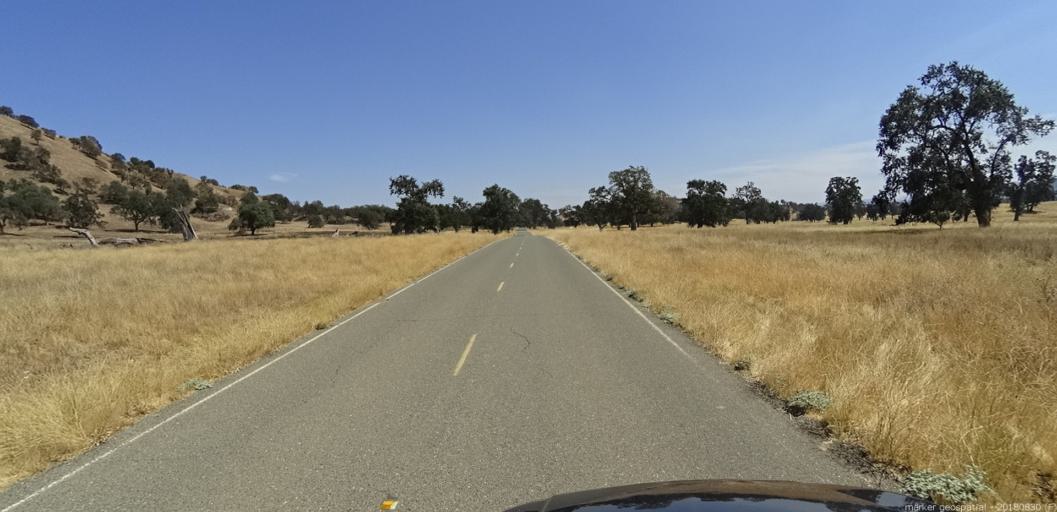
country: US
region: California
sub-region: Monterey County
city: King City
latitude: 35.9662
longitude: -121.3041
